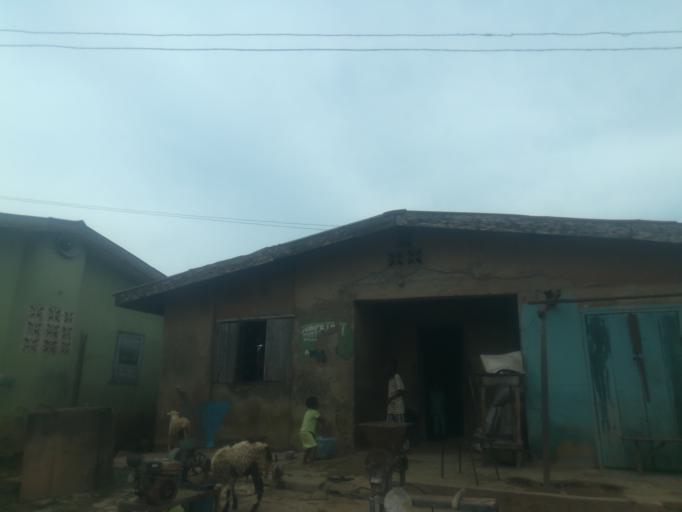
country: NG
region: Oyo
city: Ibadan
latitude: 7.3742
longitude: 3.9535
